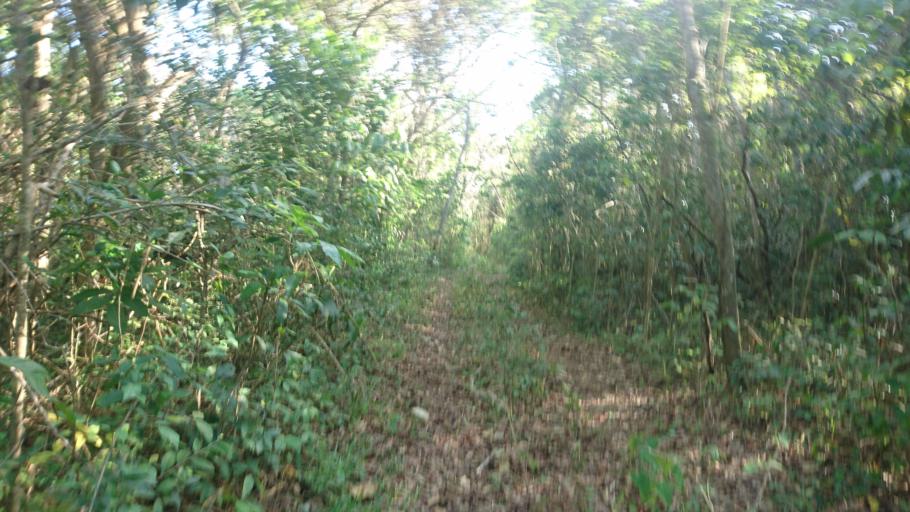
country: CU
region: Artemisa
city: Soroa
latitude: 22.8299
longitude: -82.9207
